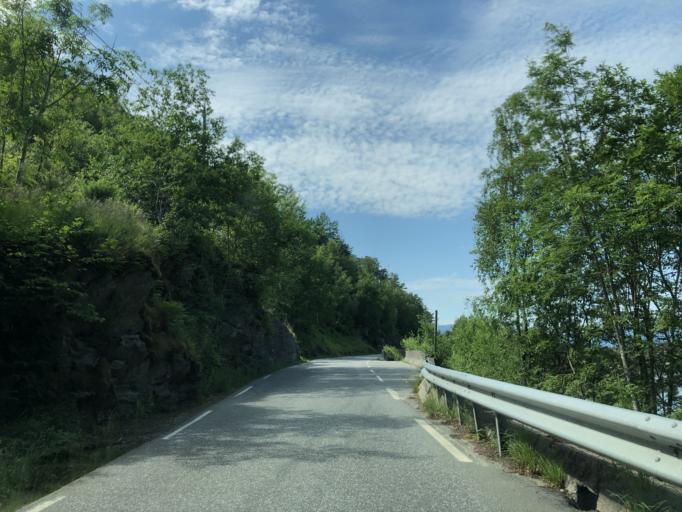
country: NO
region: Hordaland
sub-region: Jondal
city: Jondal
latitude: 60.3377
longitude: 6.3636
